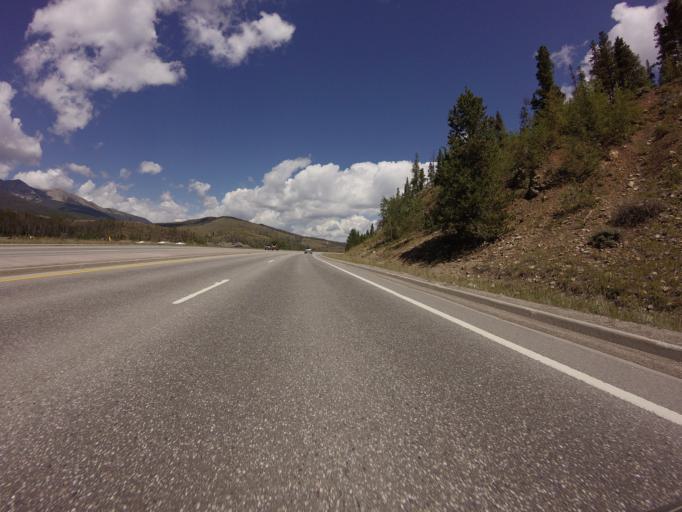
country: US
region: Colorado
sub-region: Summit County
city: Breckenridge
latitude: 39.5106
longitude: -106.0487
